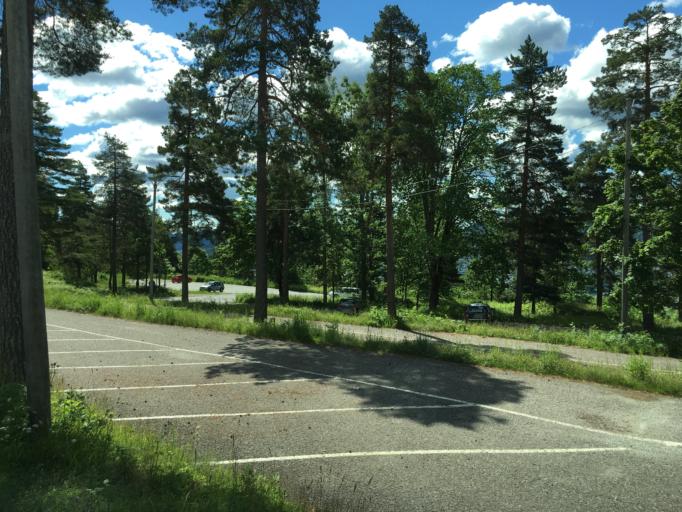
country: NO
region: Buskerud
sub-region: Drammen
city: Drammen
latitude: 59.7526
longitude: 10.2022
